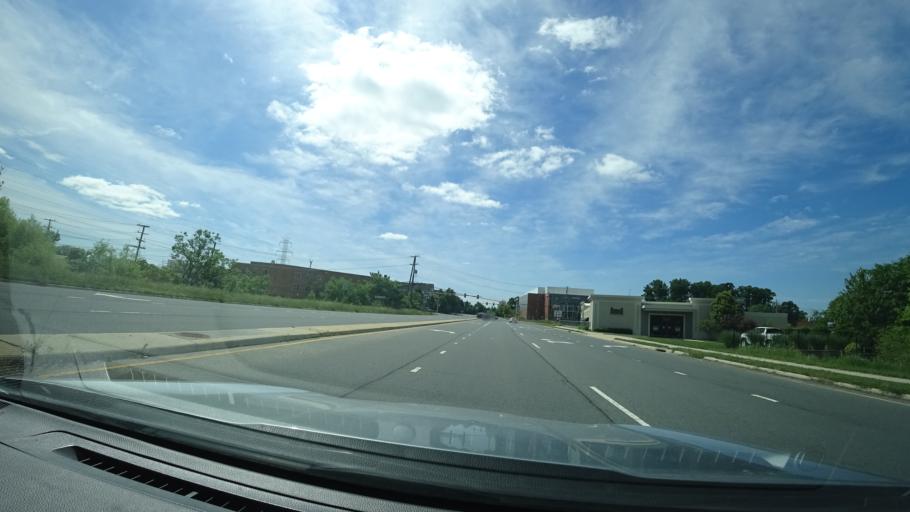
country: US
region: Virginia
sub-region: Loudoun County
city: Sterling
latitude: 39.0062
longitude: -77.4297
